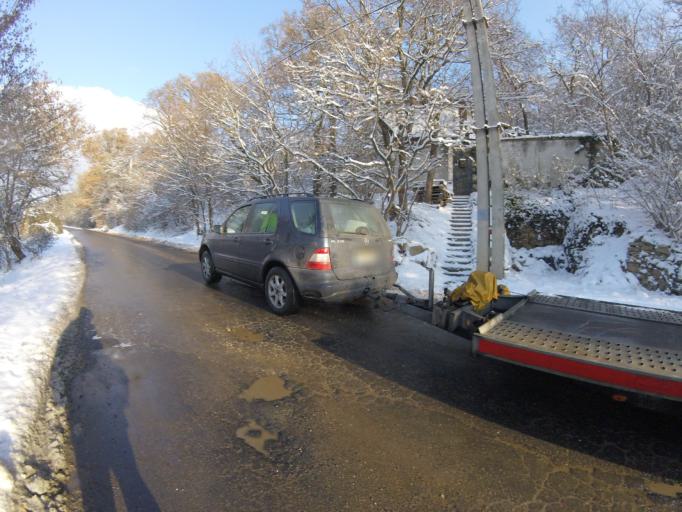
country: HU
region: Pest
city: Budakeszi
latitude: 47.4961
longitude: 18.9224
